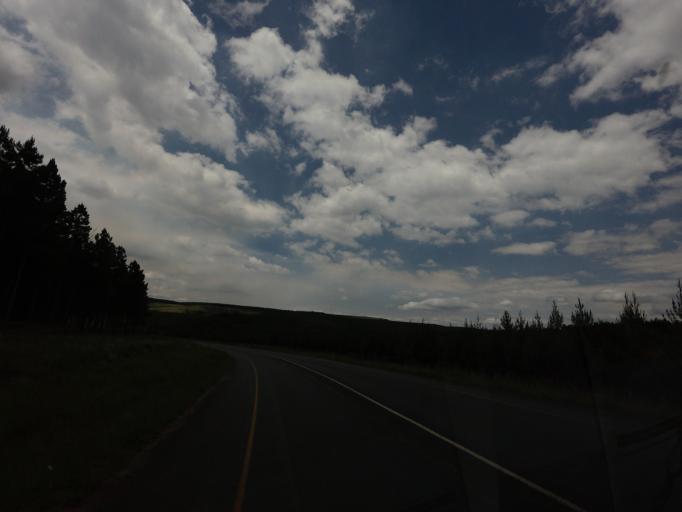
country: ZA
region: Mpumalanga
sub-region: Ehlanzeni District
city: Graksop
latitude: -24.9685
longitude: 30.8101
